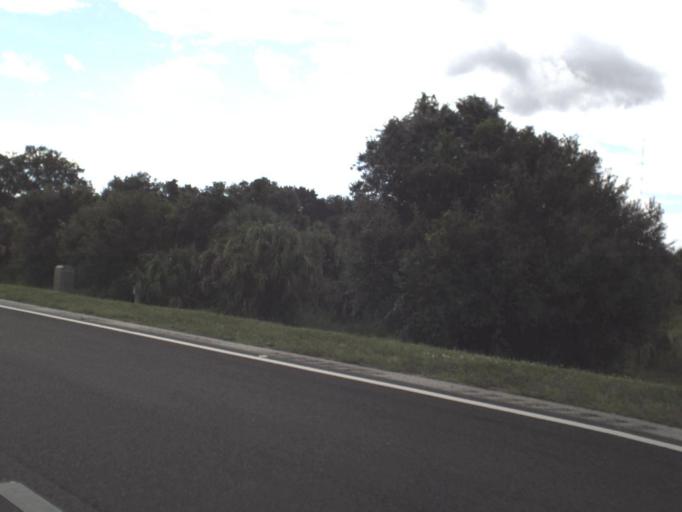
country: US
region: Florida
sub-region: Sarasota County
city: Plantation
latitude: 27.1092
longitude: -82.3775
